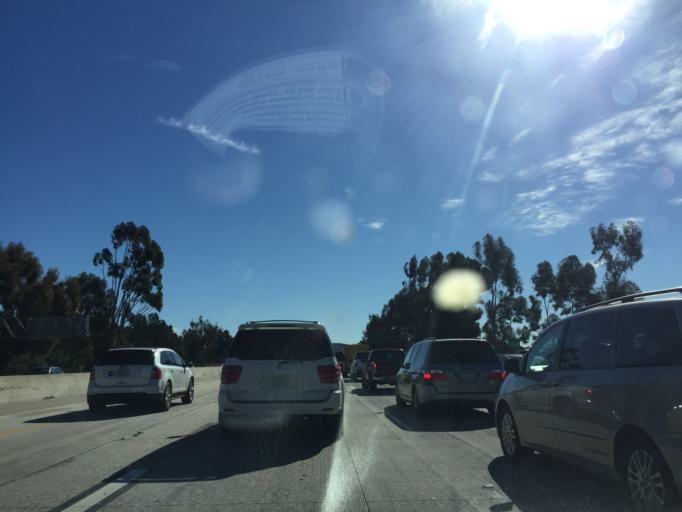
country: US
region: California
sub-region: Orange County
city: San Juan Capistrano
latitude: 33.5215
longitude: -117.6662
